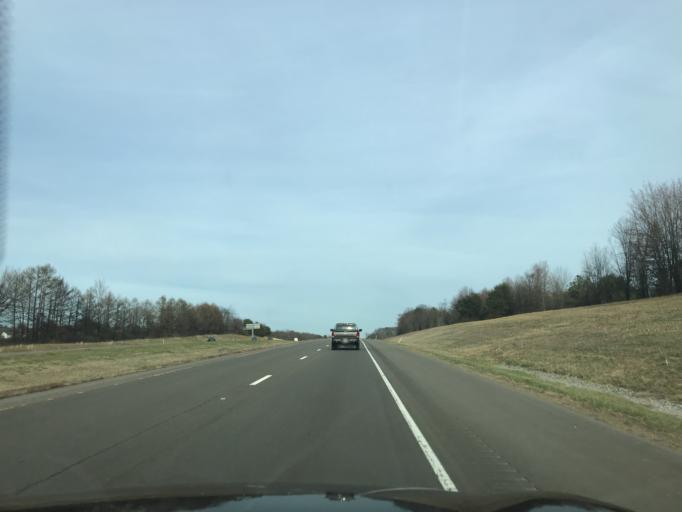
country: US
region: Pennsylvania
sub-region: Lycoming County
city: Montoursville
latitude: 41.2528
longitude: -76.8792
